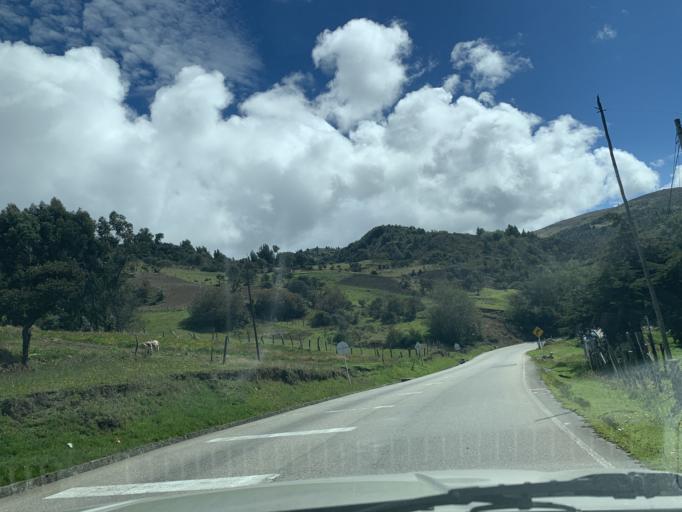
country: CO
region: Boyaca
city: Aquitania
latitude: 5.6150
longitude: -72.8788
